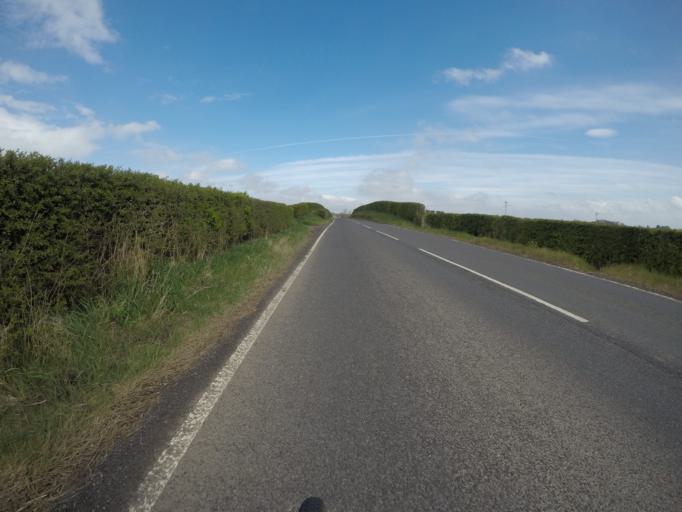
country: GB
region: Scotland
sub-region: East Ayrshire
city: Kilmaurs
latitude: 55.6573
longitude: -4.5555
